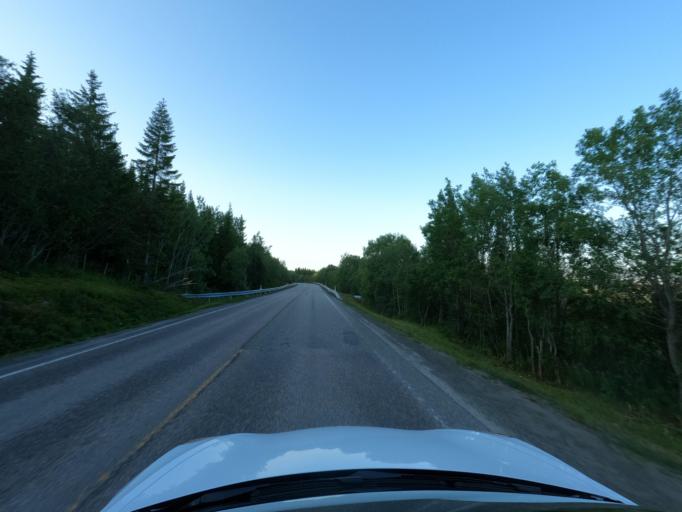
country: NO
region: Troms
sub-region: Harstad
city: Harstad
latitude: 68.7228
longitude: 16.5340
